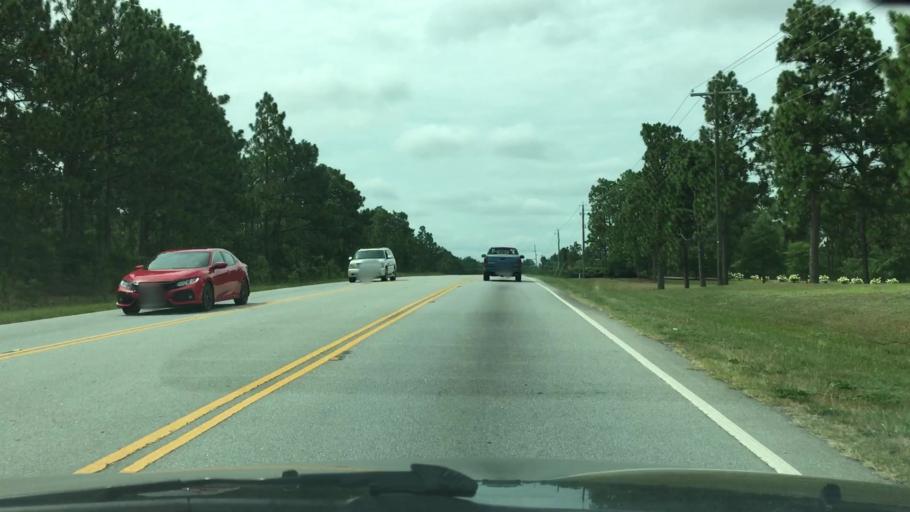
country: US
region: South Carolina
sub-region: Aiken County
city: Warrenville
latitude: 33.5457
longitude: -81.7765
